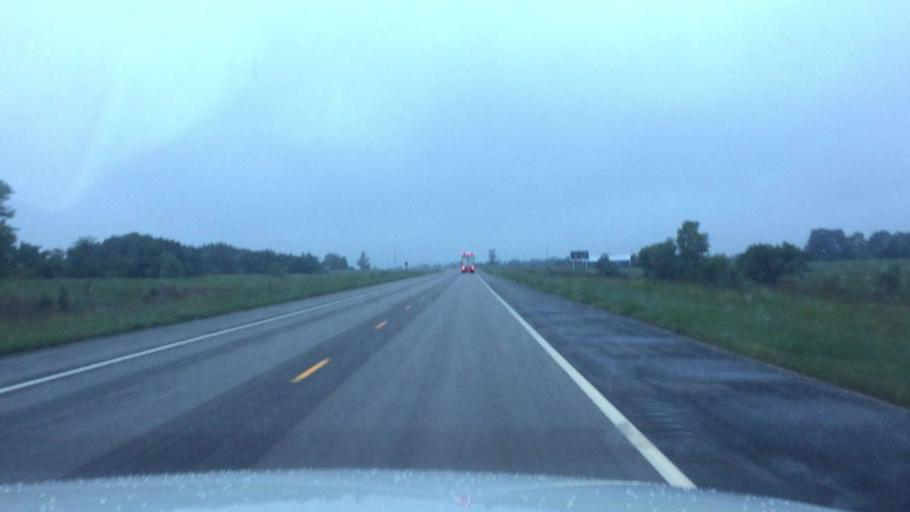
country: US
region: Kansas
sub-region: Montgomery County
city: Cherryvale
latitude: 37.4607
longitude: -95.4803
